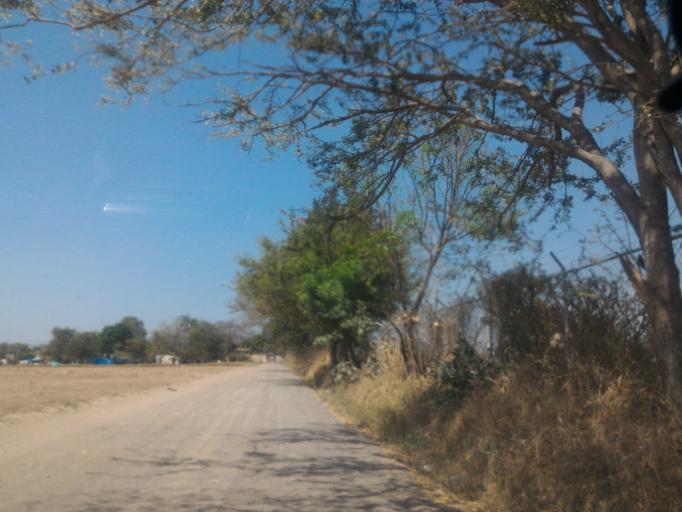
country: MX
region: Jalisco
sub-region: San Pedro Tlaquepaque
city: Paseo del Prado
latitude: 20.5647
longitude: -103.4068
